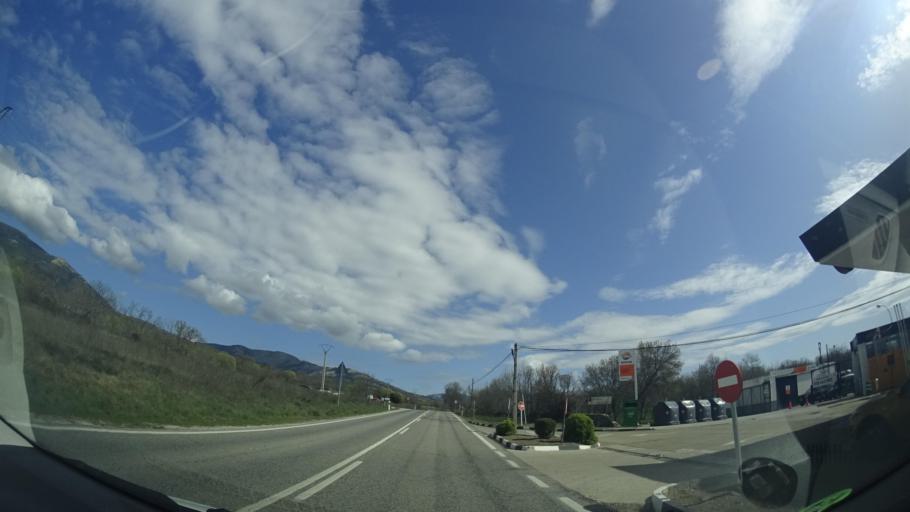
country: ES
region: Madrid
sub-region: Provincia de Madrid
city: Miraflores de la Sierra
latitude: 40.7806
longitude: -3.7746
